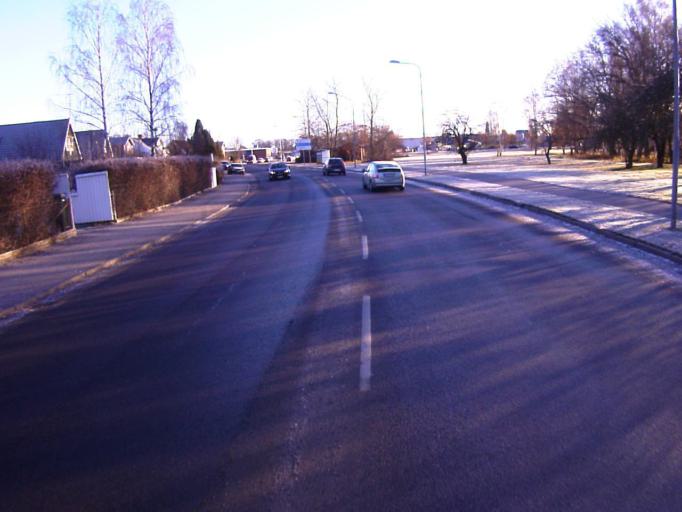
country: SE
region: Soedermanland
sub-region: Eskilstuna Kommun
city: Eskilstuna
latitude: 59.3828
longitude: 16.4967
